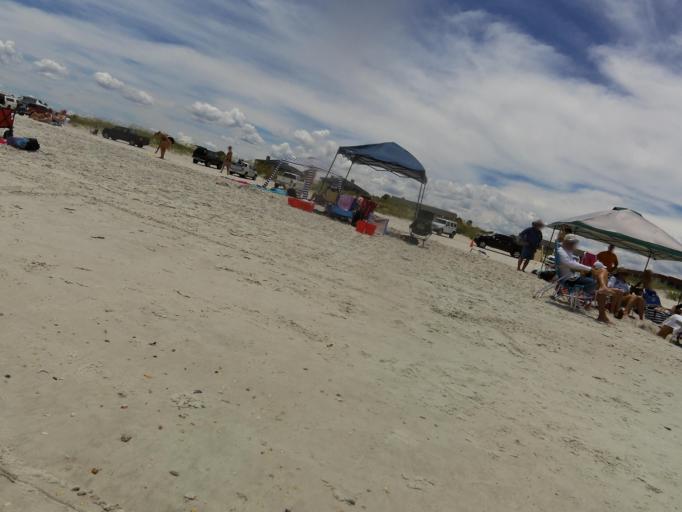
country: US
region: Florida
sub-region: Saint Johns County
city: Saint Augustine Beach
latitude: 29.8342
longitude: -81.2631
